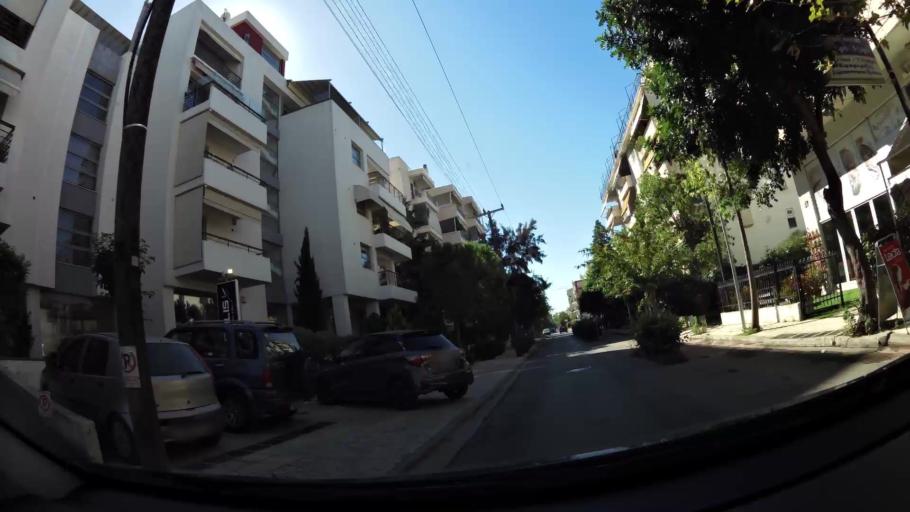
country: GR
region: Attica
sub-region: Nomarchia Athinas
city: Khalandrion
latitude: 38.0329
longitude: 23.8083
